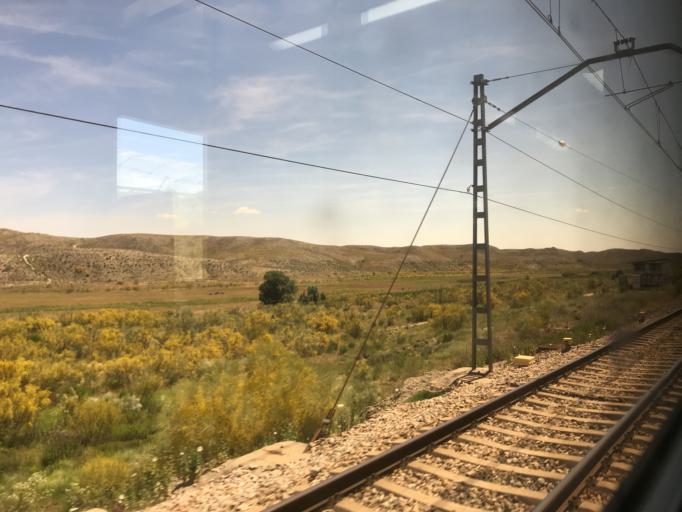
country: ES
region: Madrid
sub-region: Provincia de Madrid
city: Ciempozuelos
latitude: 40.1744
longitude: -3.6267
